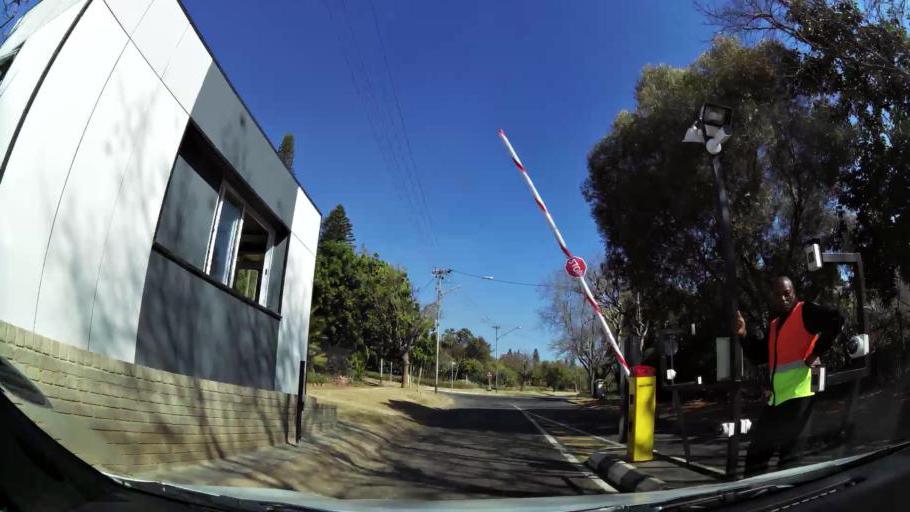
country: ZA
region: Gauteng
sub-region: City of Tshwane Metropolitan Municipality
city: Pretoria
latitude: -25.7774
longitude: 28.2252
